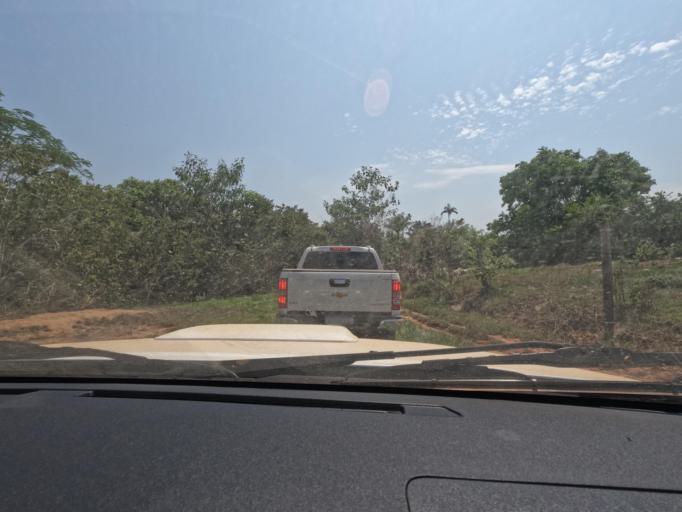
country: BR
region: Rondonia
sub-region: Porto Velho
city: Porto Velho
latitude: -8.6678
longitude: -64.2666
